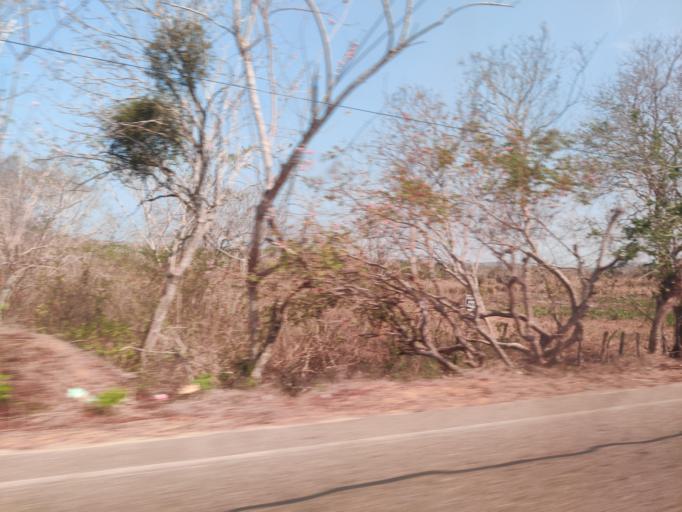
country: CO
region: Bolivar
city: Turbana
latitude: 10.2167
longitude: -75.5903
